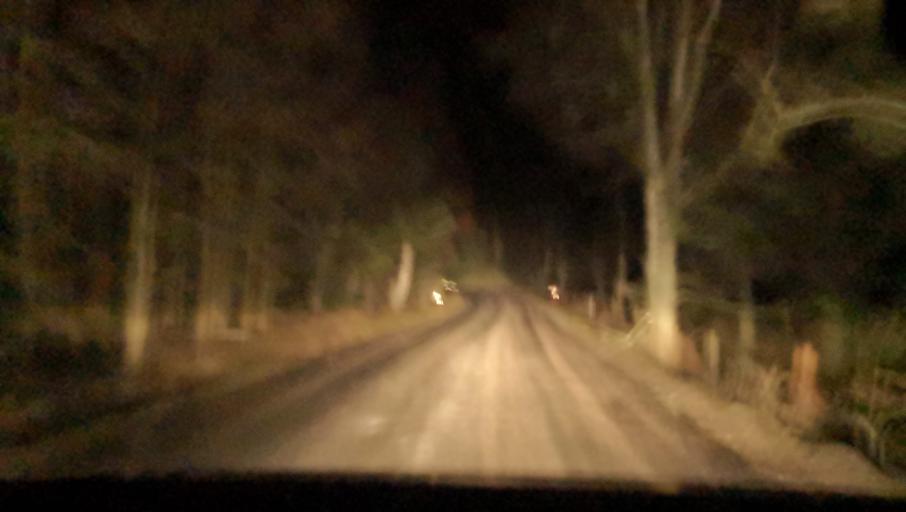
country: SE
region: Vaestmanland
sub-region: Vasteras
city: Tillberga
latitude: 59.6705
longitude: 16.6315
